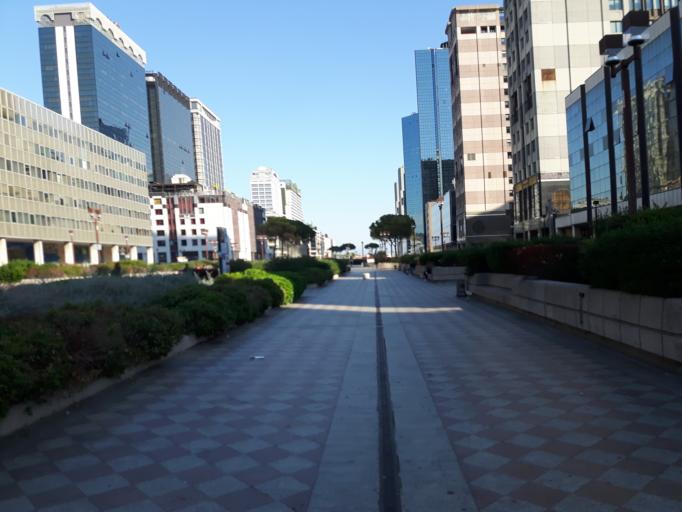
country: IT
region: Campania
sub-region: Provincia di Napoli
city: Napoli
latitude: 40.8565
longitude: 14.2778
